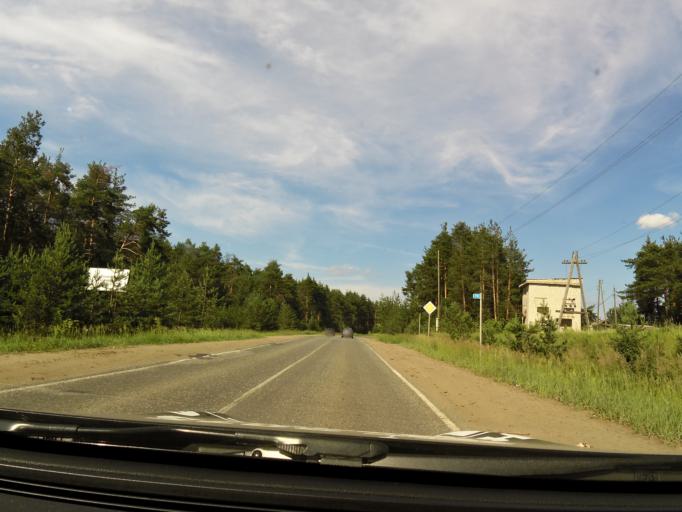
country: RU
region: Kirov
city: Belaya Kholunitsa
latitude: 58.8504
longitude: 50.8288
